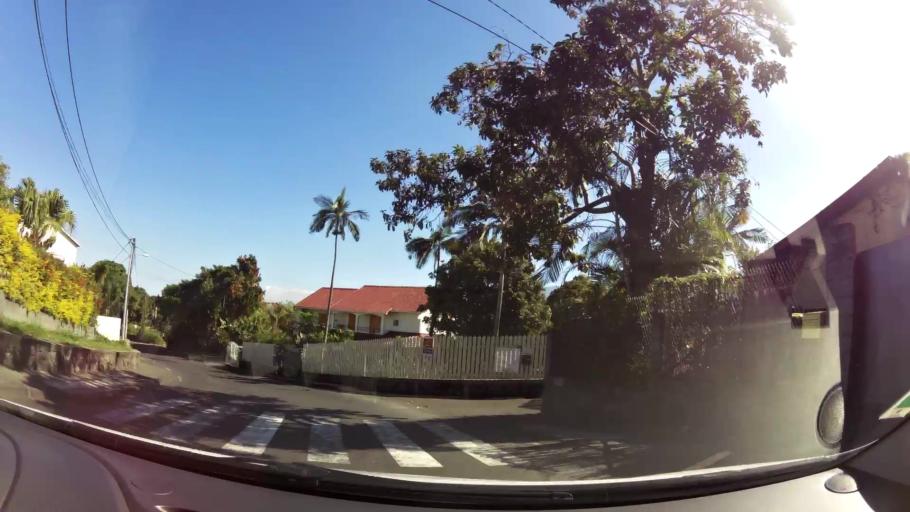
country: RE
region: Reunion
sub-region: Reunion
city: Le Tampon
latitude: -21.2680
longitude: 55.5117
